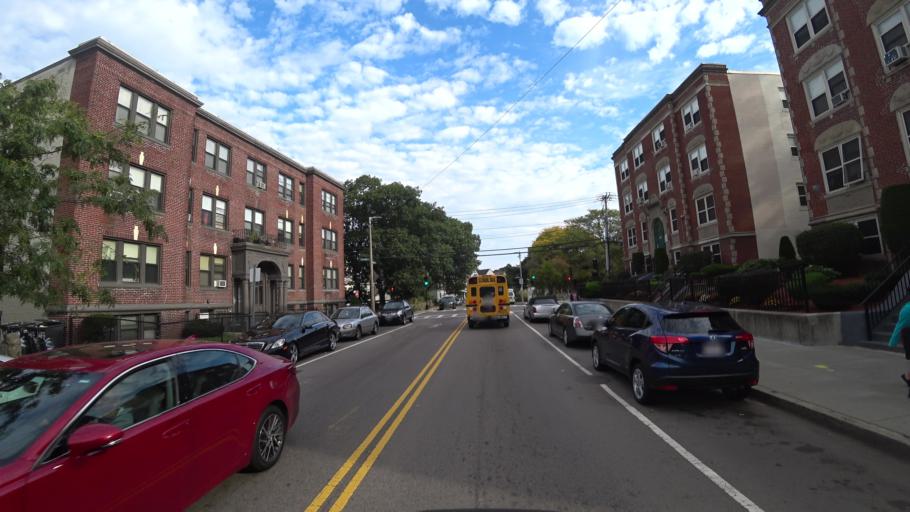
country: US
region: Massachusetts
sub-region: Suffolk County
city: Jamaica Plain
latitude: 42.3179
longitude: -71.0911
